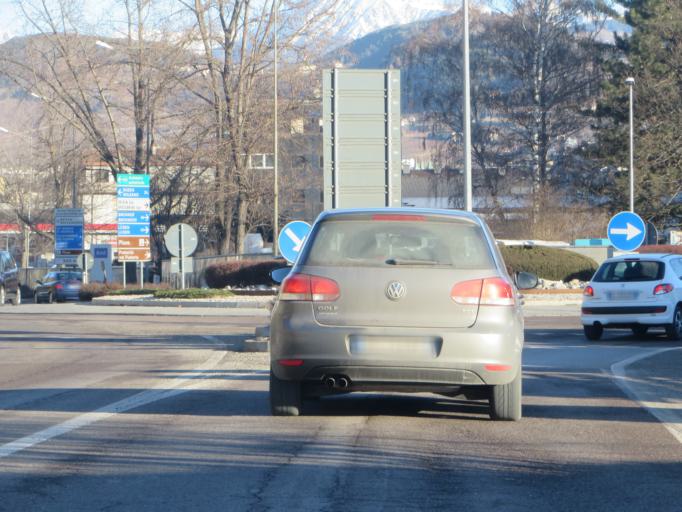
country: IT
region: Trentino-Alto Adige
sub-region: Bolzano
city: Bressanone
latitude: 46.7020
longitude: 11.6480
